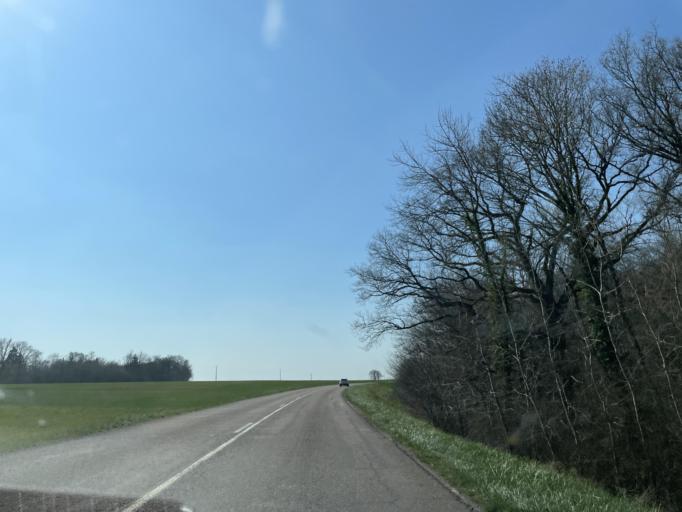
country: FR
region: Bourgogne
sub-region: Departement de la Cote-d'Or
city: Semur-en-Auxois
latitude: 47.4472
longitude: 4.3255
